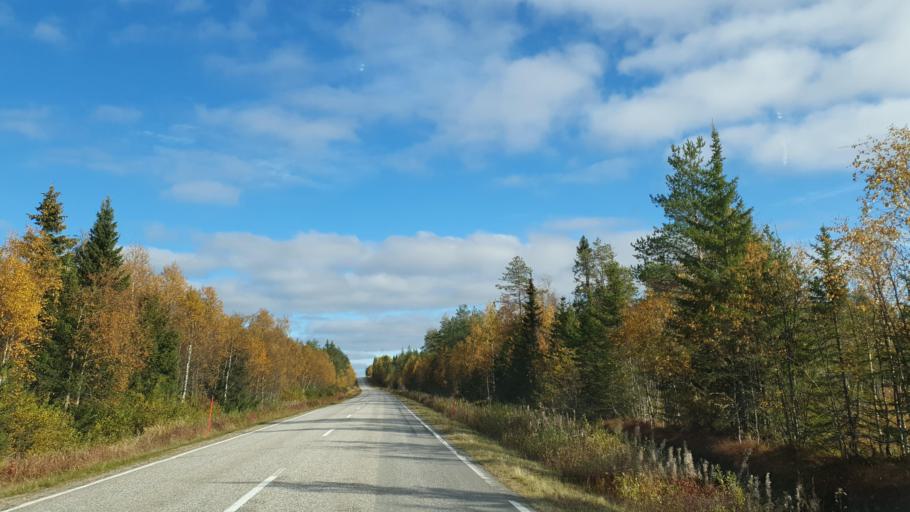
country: FI
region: Kainuu
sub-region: Kehys-Kainuu
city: Puolanka
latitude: 64.8246
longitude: 28.0011
